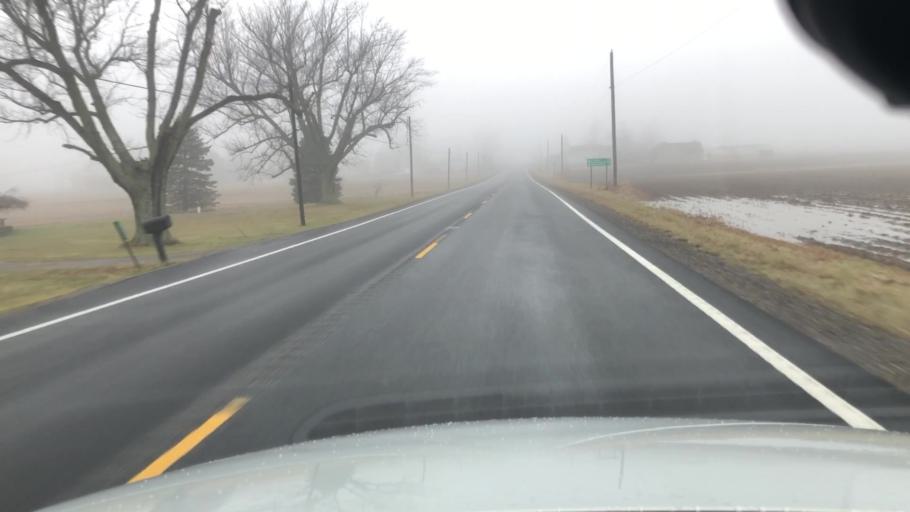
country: US
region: Ohio
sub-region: Logan County
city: Lakeview
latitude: 40.6009
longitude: -83.8770
